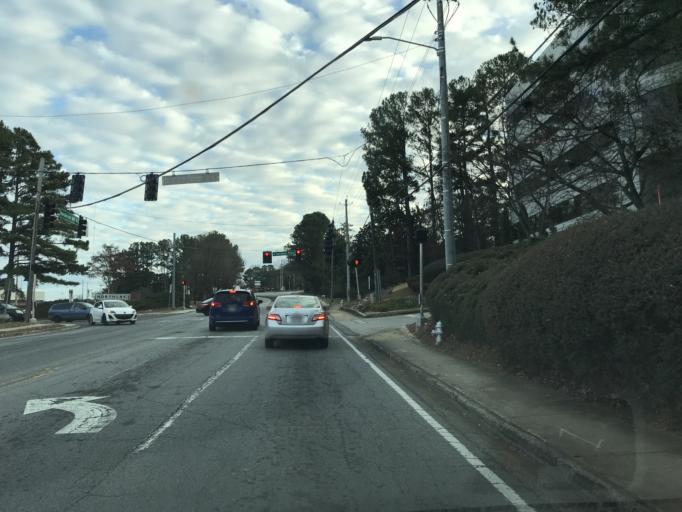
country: US
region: Georgia
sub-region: DeKalb County
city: Tucker
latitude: 33.8528
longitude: -84.2592
